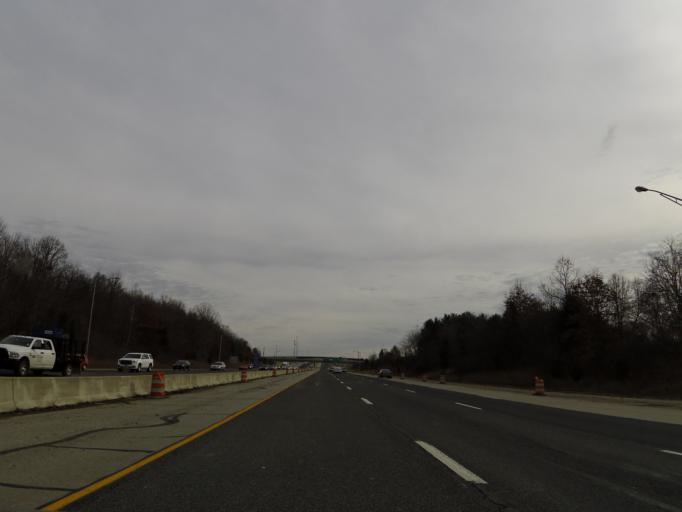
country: US
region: Indiana
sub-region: Marion County
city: Meridian Hills
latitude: 39.9301
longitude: -86.1705
